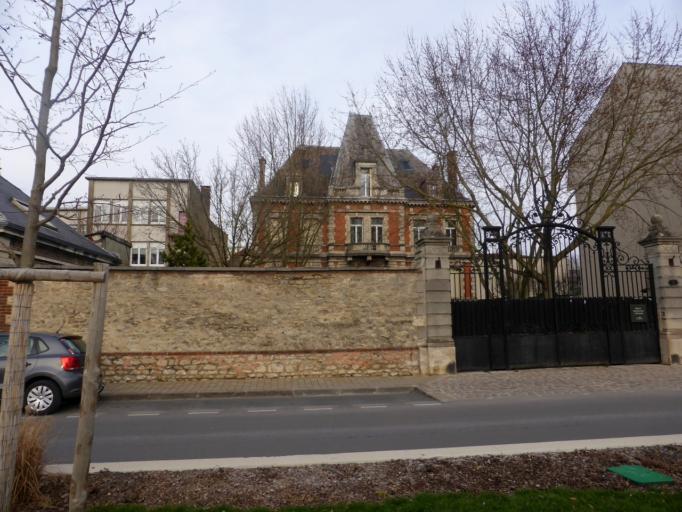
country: FR
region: Champagne-Ardenne
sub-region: Departement de l'Aube
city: Troyes
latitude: 48.2966
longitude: 4.0807
